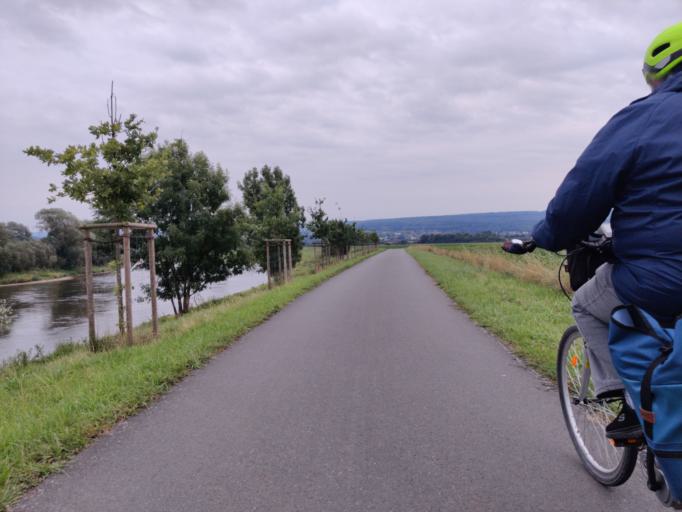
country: DE
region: North Rhine-Westphalia
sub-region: Regierungsbezirk Detmold
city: Hoexter
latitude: 51.8029
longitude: 9.4069
